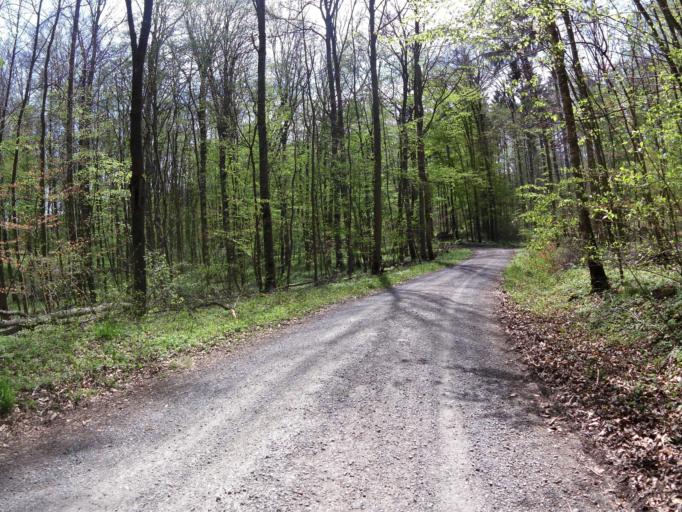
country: DE
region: Bavaria
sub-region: Regierungsbezirk Unterfranken
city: Rimpar
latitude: 49.8626
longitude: 9.9896
